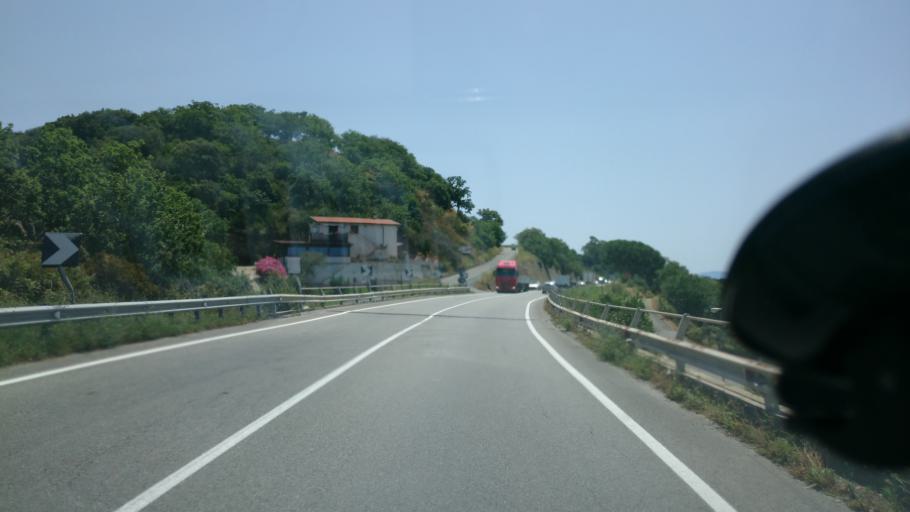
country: IT
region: Calabria
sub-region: Provincia di Cosenza
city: Cittadella del Capo
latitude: 39.5444
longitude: 15.8886
